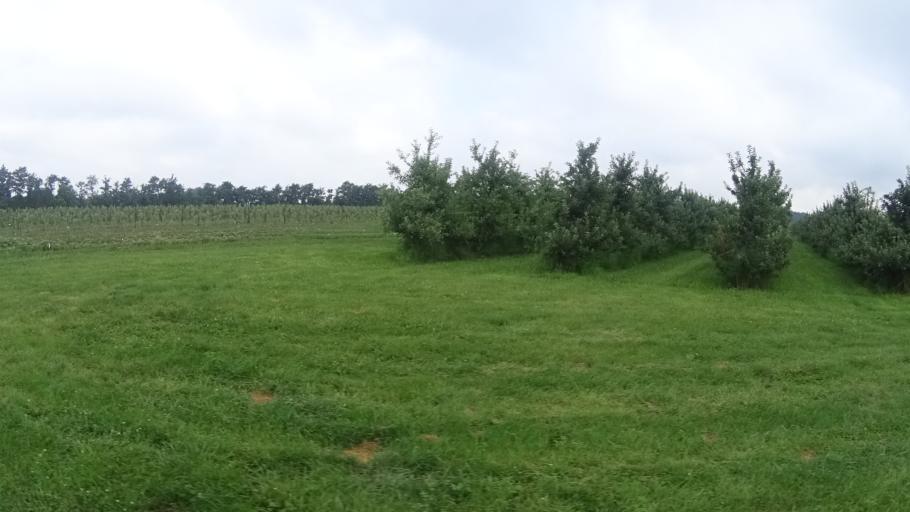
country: US
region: Ohio
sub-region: Huron County
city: Wakeman
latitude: 41.3008
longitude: -82.4951
